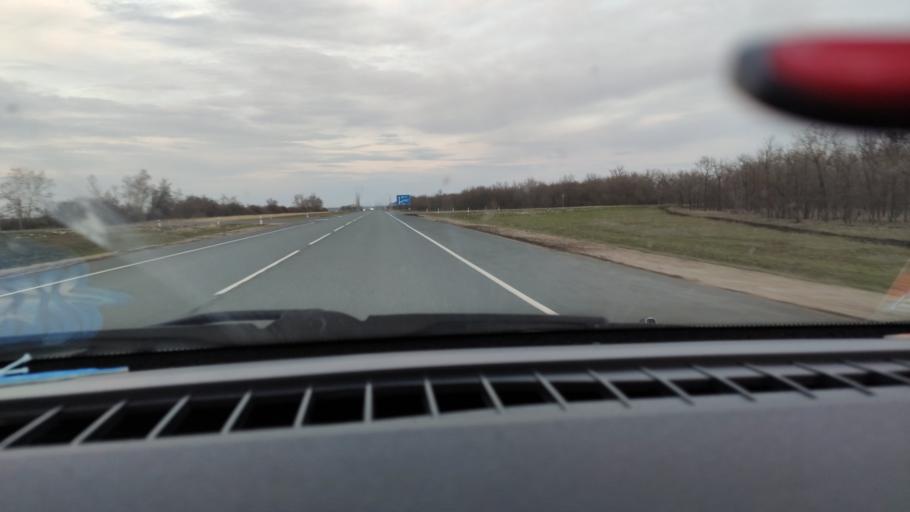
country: RU
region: Saratov
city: Yelshanka
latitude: 51.8196
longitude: 46.3551
